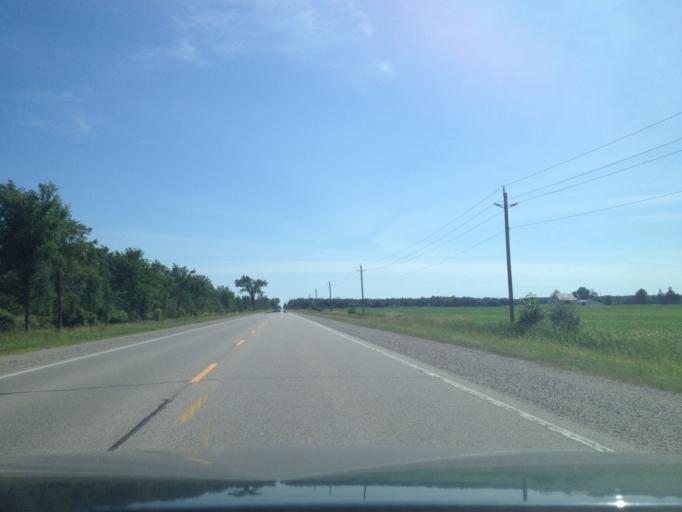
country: CA
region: Ontario
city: Stratford
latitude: 43.4739
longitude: -80.8992
